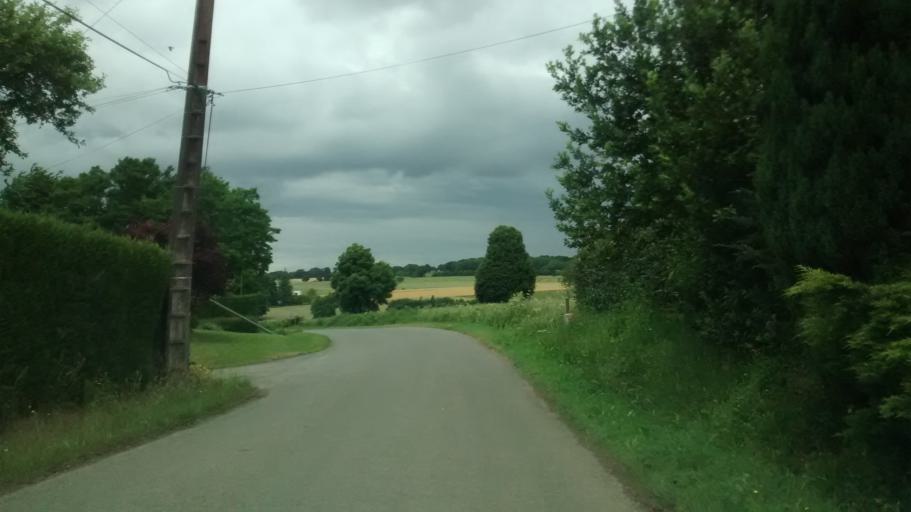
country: FR
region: Brittany
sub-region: Departement d'Ille-et-Vilaine
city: Sixt-sur-Aff
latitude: 47.7927
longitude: -2.1057
